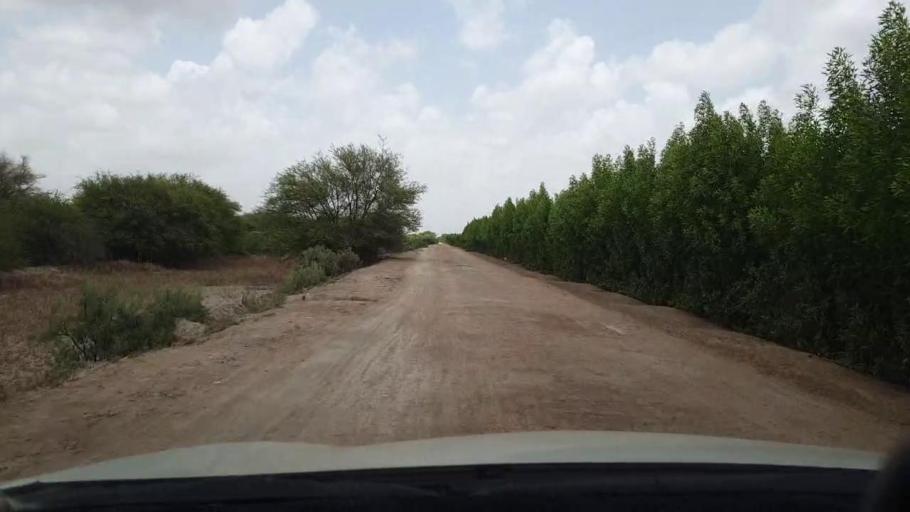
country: PK
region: Sindh
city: Kadhan
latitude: 24.3603
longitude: 68.9556
